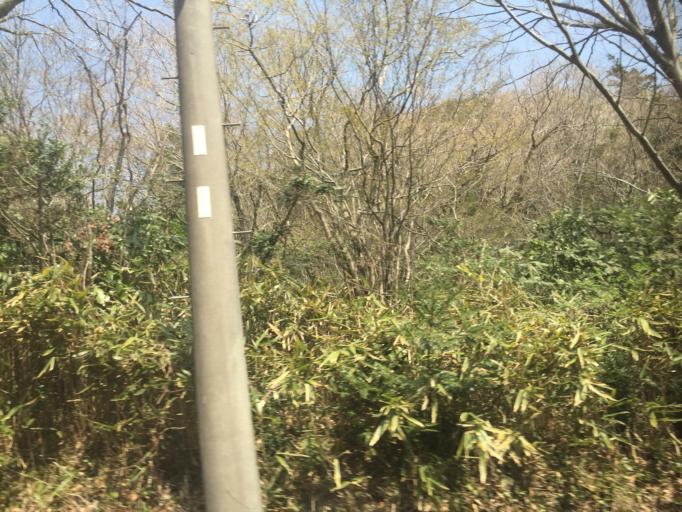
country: JP
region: Shizuoka
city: Ito
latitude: 34.9013
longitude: 139.0903
